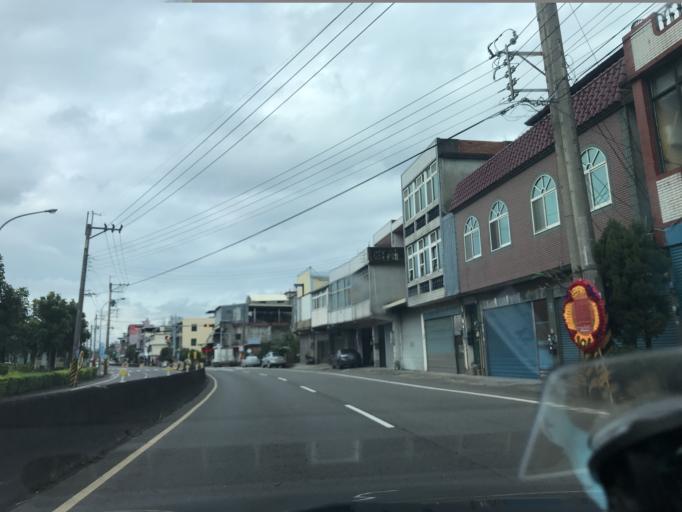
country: TW
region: Taiwan
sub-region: Hsinchu
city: Zhubei
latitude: 24.8071
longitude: 121.0484
